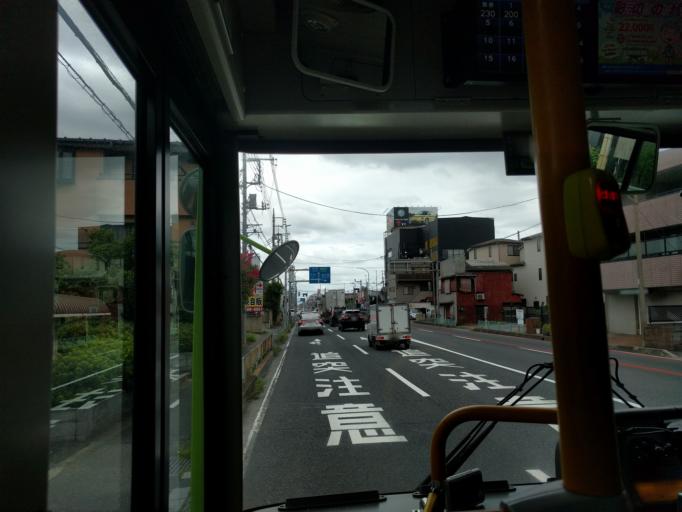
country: JP
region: Saitama
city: Kawaguchi
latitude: 35.8053
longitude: 139.7331
